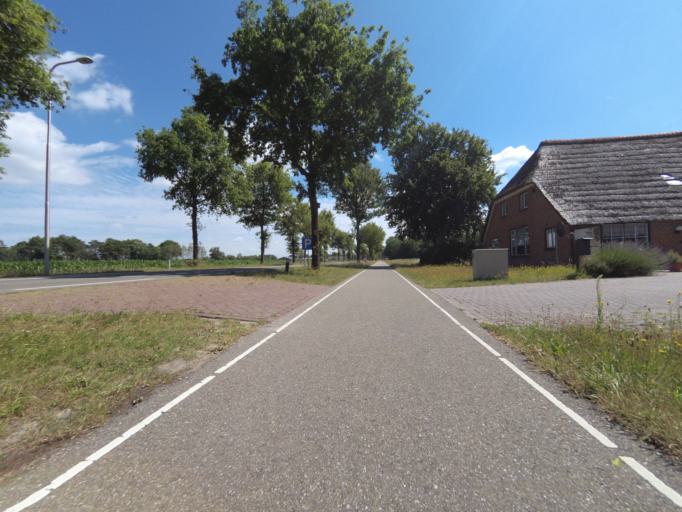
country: NL
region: Gelderland
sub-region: Gemeente Voorst
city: Voorst
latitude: 52.1773
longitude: 6.0801
